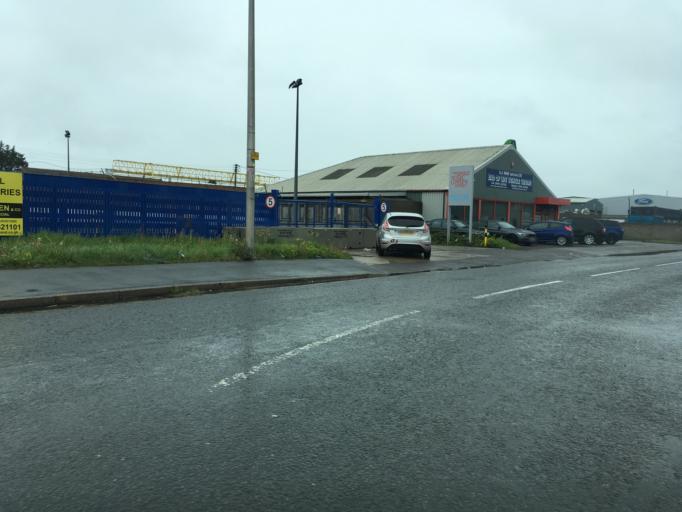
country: GB
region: England
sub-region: North Somerset
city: Weston-super-Mare
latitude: 51.3415
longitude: -2.9633
